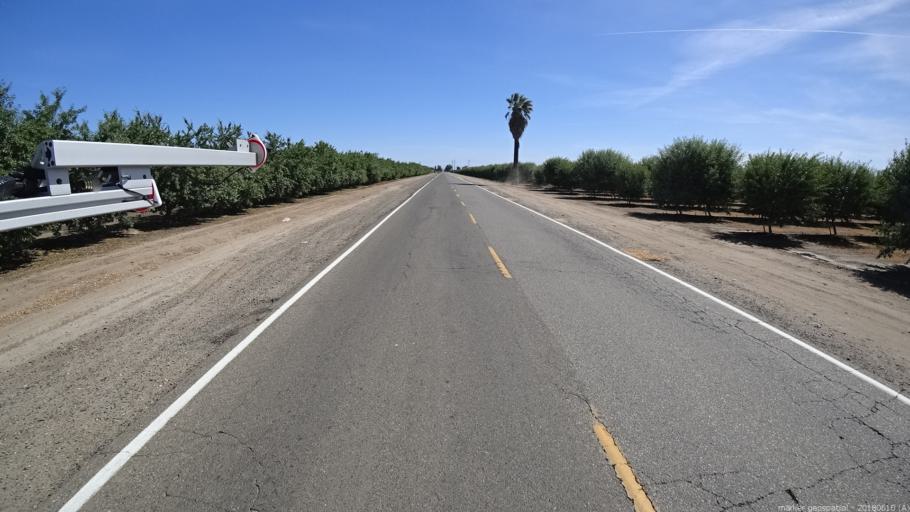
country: US
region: California
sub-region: Madera County
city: Chowchilla
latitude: 37.0280
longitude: -120.3448
